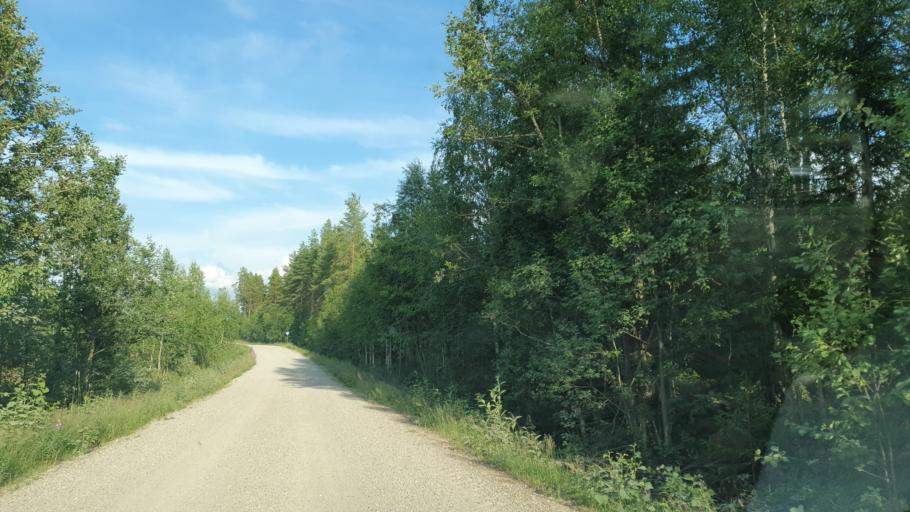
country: FI
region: Kainuu
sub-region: Kehys-Kainuu
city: Kuhmo
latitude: 64.2880
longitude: 29.7441
